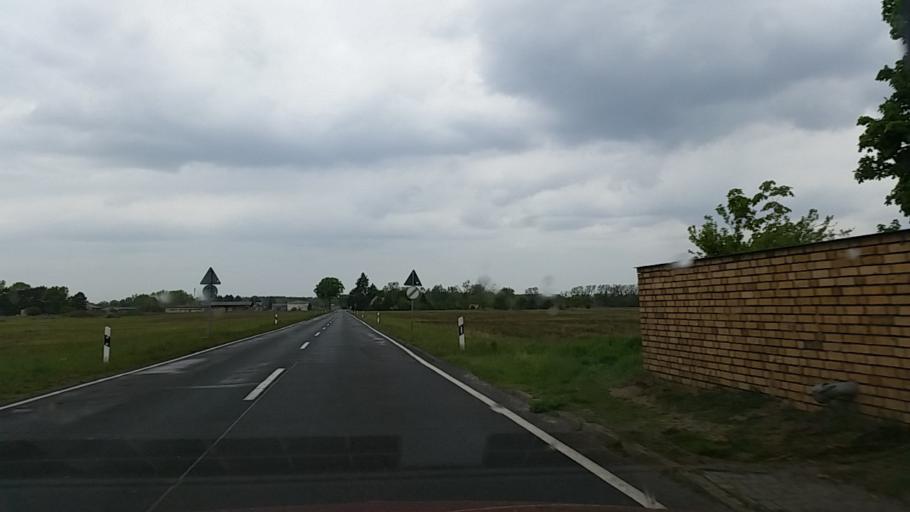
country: DE
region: Brandenburg
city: Spreenhagen
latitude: 52.3365
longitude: 13.8930
